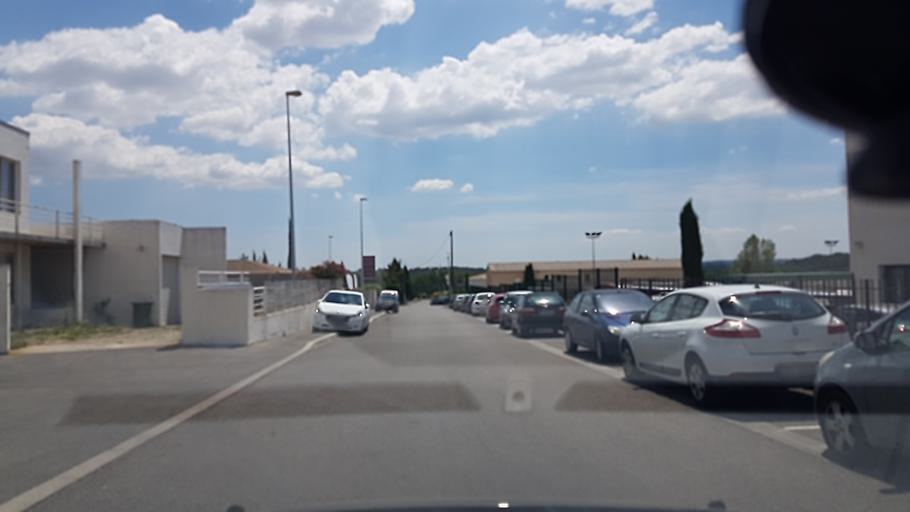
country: FR
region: Provence-Alpes-Cote d'Azur
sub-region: Departement des Bouches-du-Rhone
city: Eguilles
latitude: 43.5471
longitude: 5.3628
